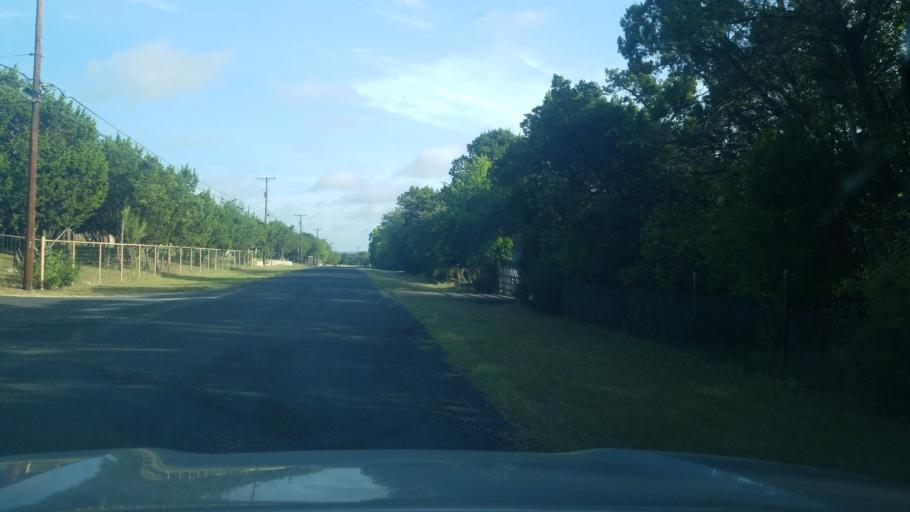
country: US
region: Texas
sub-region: Bexar County
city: Timberwood Park
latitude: 29.7000
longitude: -98.5118
